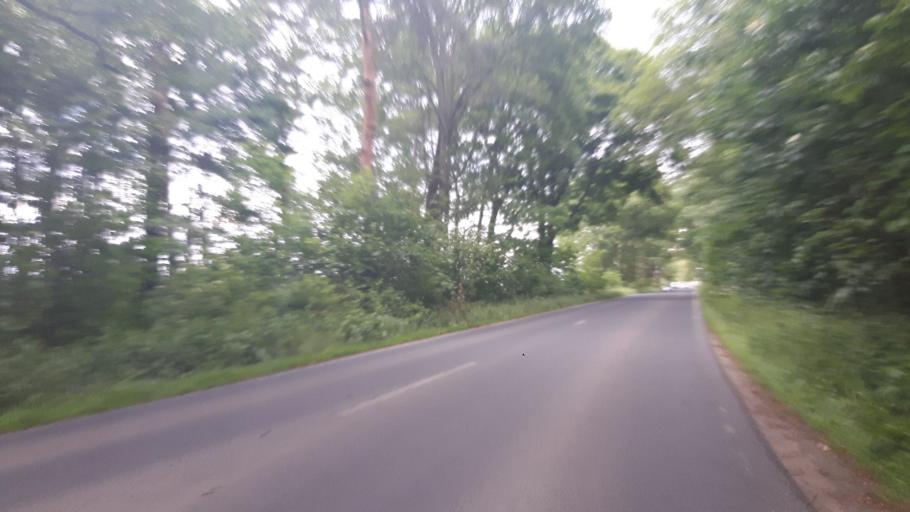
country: DE
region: Brandenburg
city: Bernau bei Berlin
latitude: 52.6519
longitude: 13.5943
